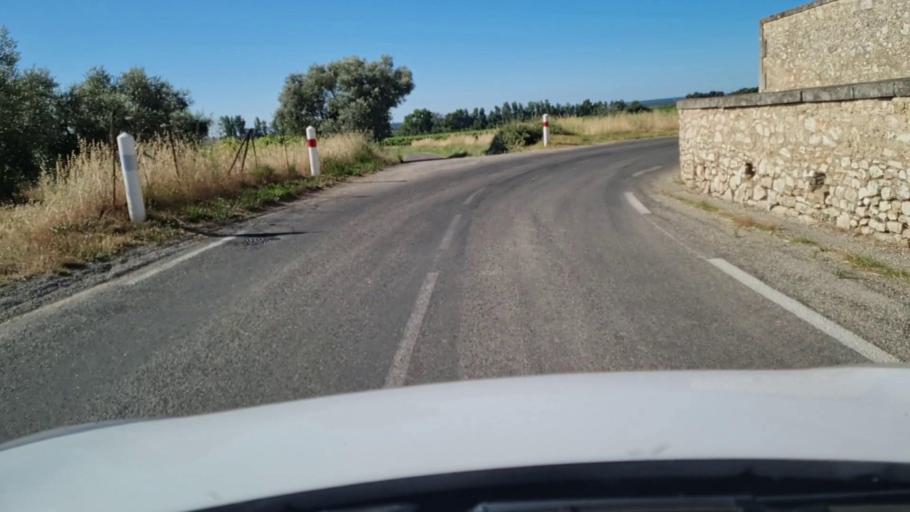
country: FR
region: Languedoc-Roussillon
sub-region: Departement du Gard
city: Sommieres
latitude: 43.8034
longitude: 4.0399
